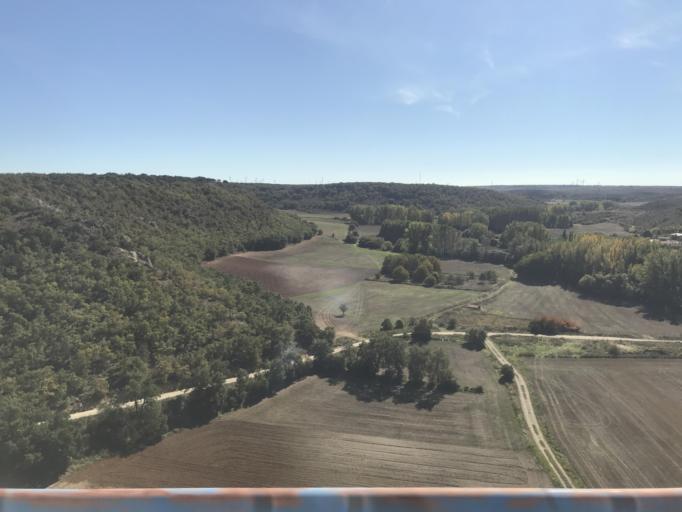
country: ES
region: Castille and Leon
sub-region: Provincia de Soria
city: Arcos de Jalon
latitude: 41.1316
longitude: -2.3338
